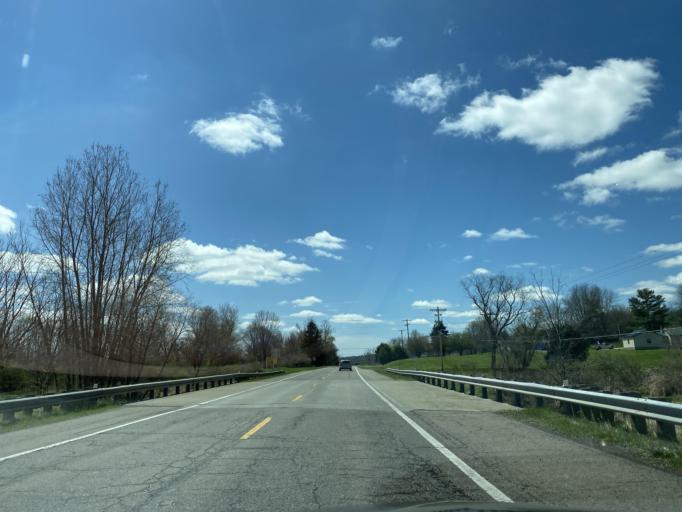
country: US
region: Ohio
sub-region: Wayne County
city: Shreve
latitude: 40.7237
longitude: -81.9981
